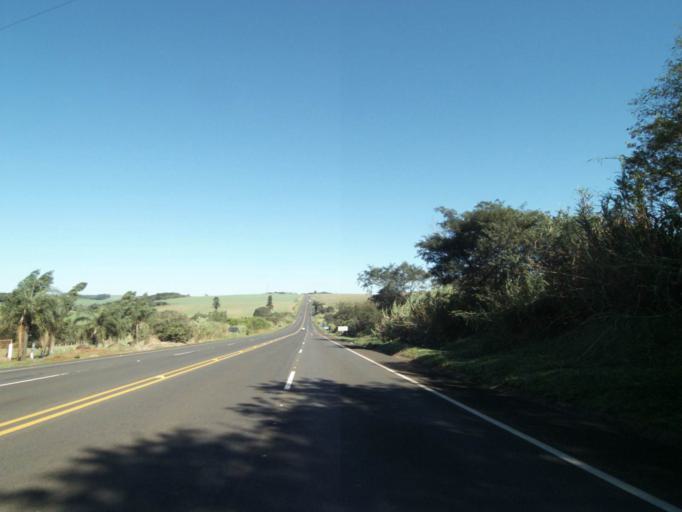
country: BR
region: Parana
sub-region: Arapongas
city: Arapongas
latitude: -23.4504
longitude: -51.5542
